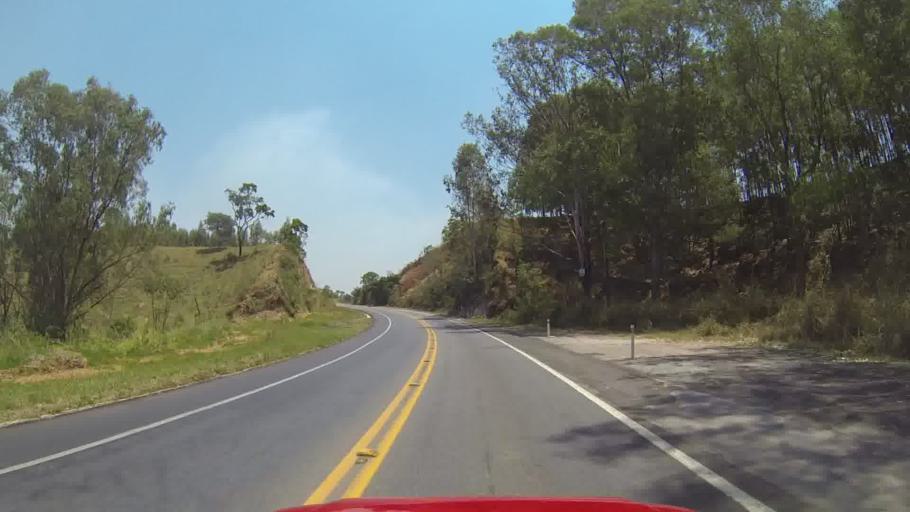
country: BR
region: Minas Gerais
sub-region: Itapecerica
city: Itapecerica
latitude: -20.3428
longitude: -45.2506
